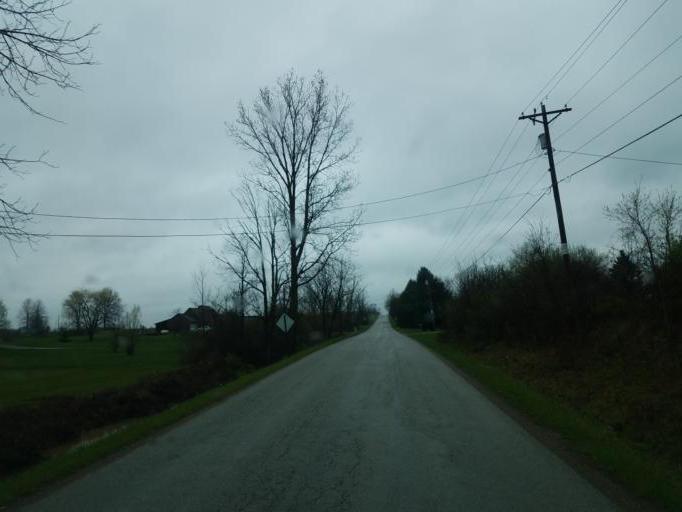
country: US
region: Ohio
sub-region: Morrow County
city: Mount Gilead
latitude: 40.4437
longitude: -82.7849
